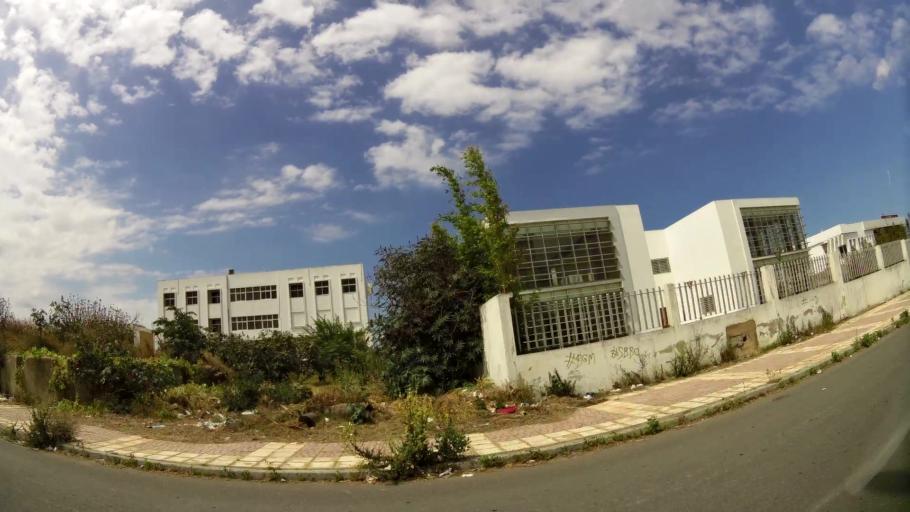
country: MA
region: Gharb-Chrarda-Beni Hssen
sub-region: Kenitra Province
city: Kenitra
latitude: 34.2529
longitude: -6.5988
